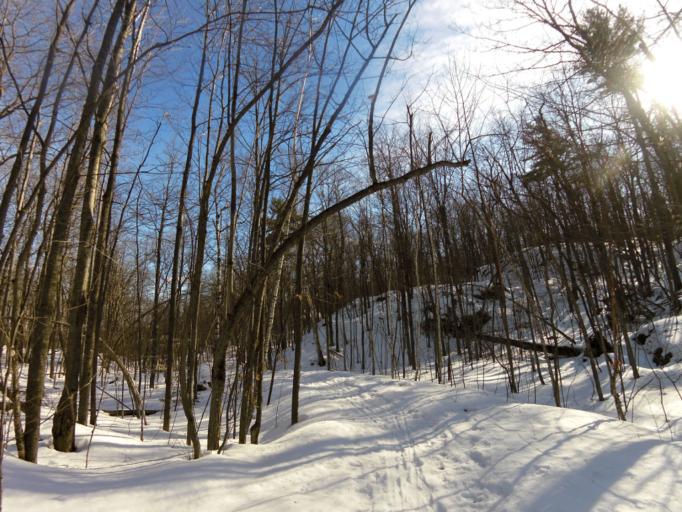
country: CA
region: Quebec
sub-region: Outaouais
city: Gatineau
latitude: 45.4698
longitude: -75.7954
